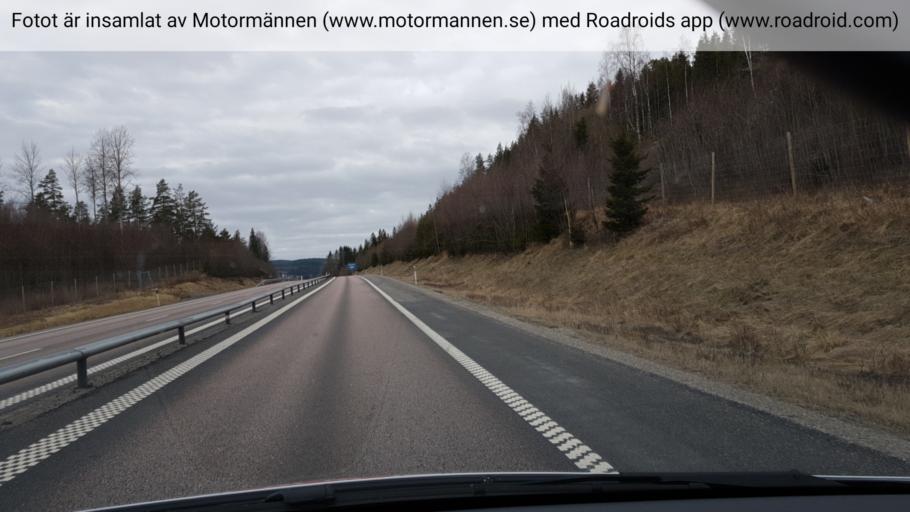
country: SE
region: Vaesternorrland
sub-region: OErnskoeldsviks Kommun
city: Ornskoldsvik
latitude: 63.3137
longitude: 18.8170
